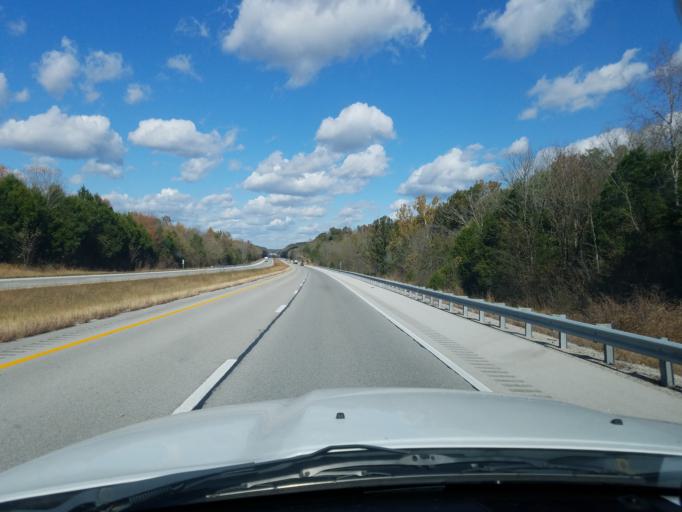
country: US
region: Kentucky
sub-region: Butler County
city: Morgantown
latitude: 37.1215
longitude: -86.6427
